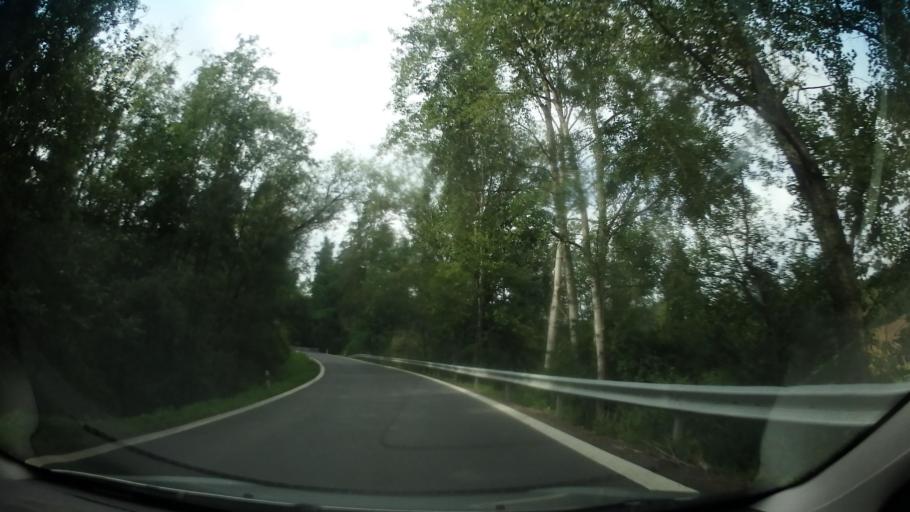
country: CZ
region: Central Bohemia
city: Neveklov
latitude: 49.7537
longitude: 14.5754
